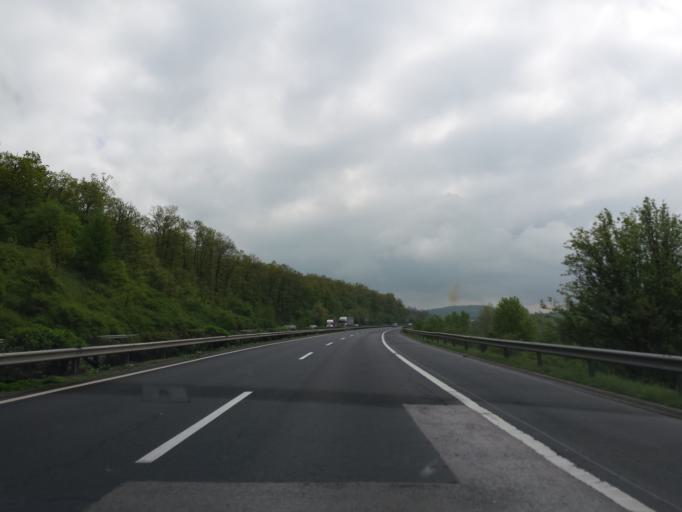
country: HU
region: Komarom-Esztergom
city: Tarjan
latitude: 47.5705
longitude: 18.4752
